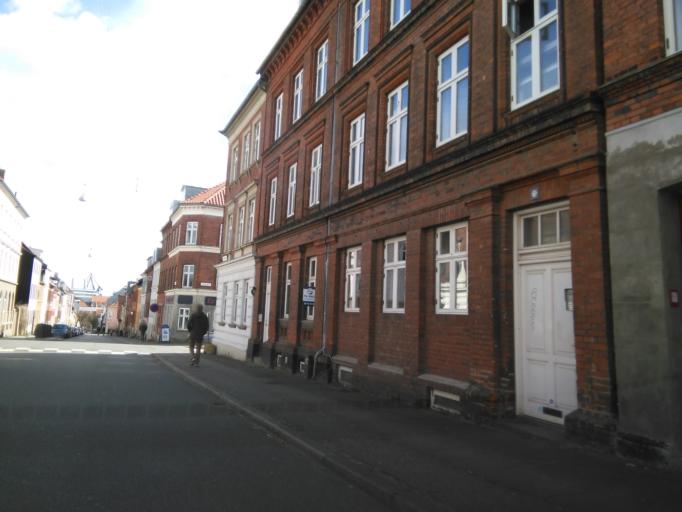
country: DK
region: Central Jutland
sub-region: Arhus Kommune
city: Arhus
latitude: 56.1628
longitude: 10.2057
